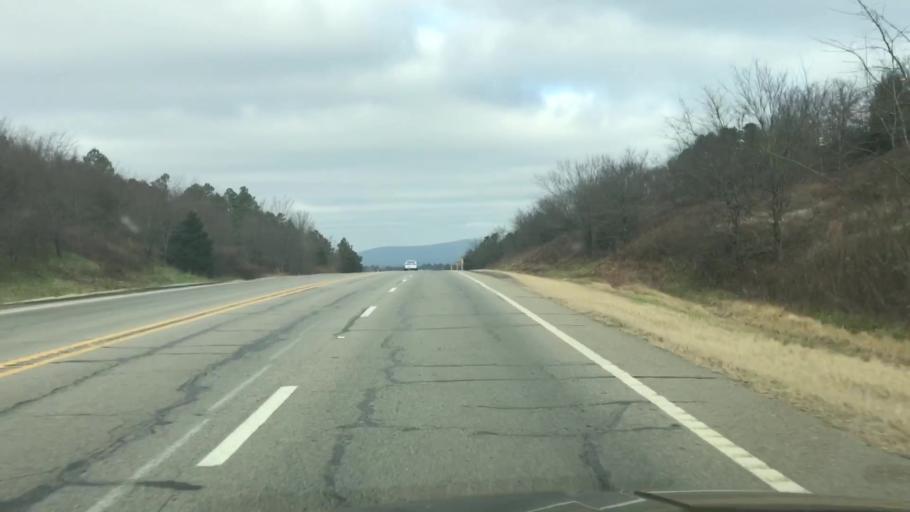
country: US
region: Arkansas
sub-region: Scott County
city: Waldron
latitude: 34.8624
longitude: -94.0721
